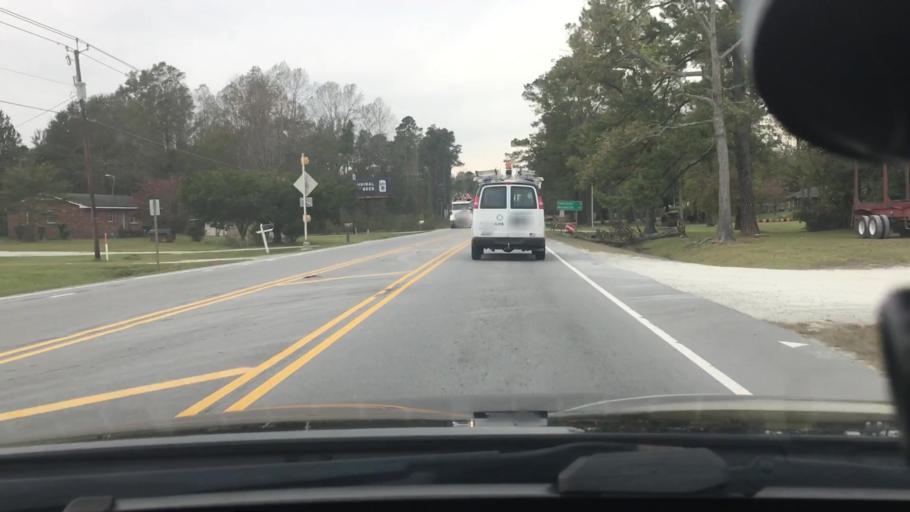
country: US
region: North Carolina
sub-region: Craven County
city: Vanceboro
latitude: 35.2506
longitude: -77.0898
